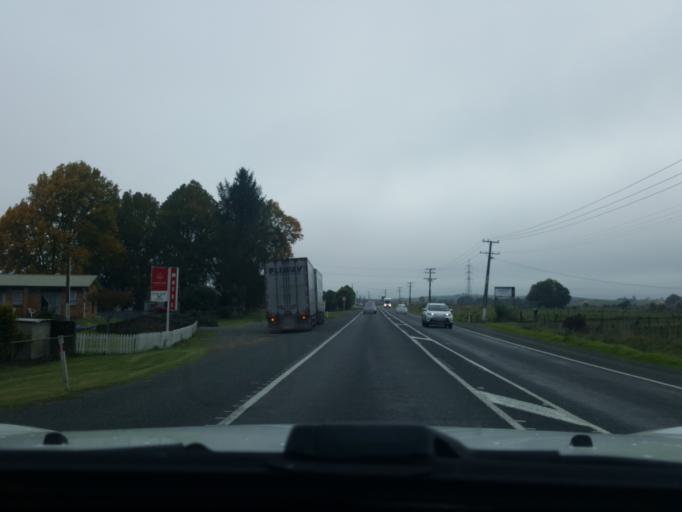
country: NZ
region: Waikato
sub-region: Waikato District
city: Te Kauwhata
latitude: -37.5234
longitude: 175.1607
